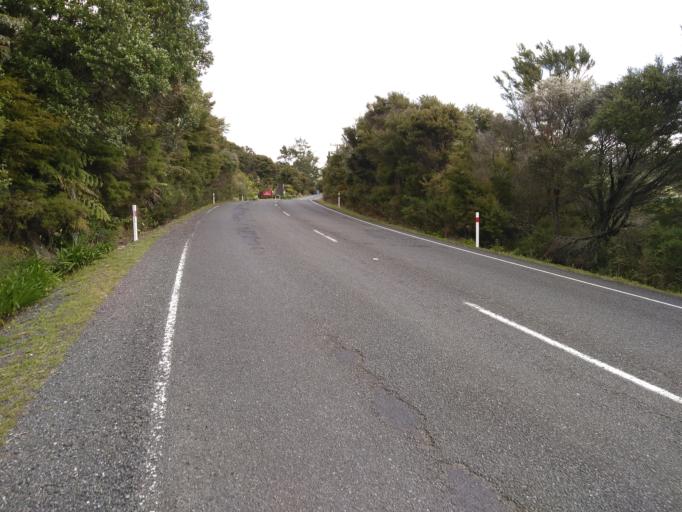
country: NZ
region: Northland
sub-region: Far North District
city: Paihia
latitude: -35.2826
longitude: 174.1474
